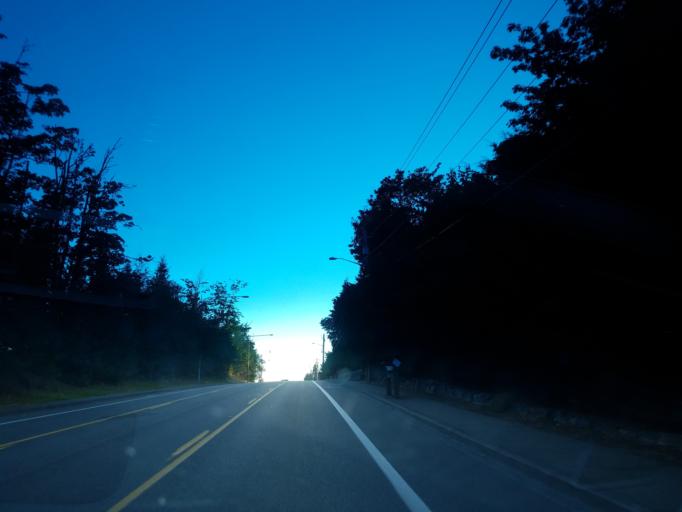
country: US
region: Washington
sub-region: King County
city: City of Sammamish
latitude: 47.6018
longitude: -122.0305
